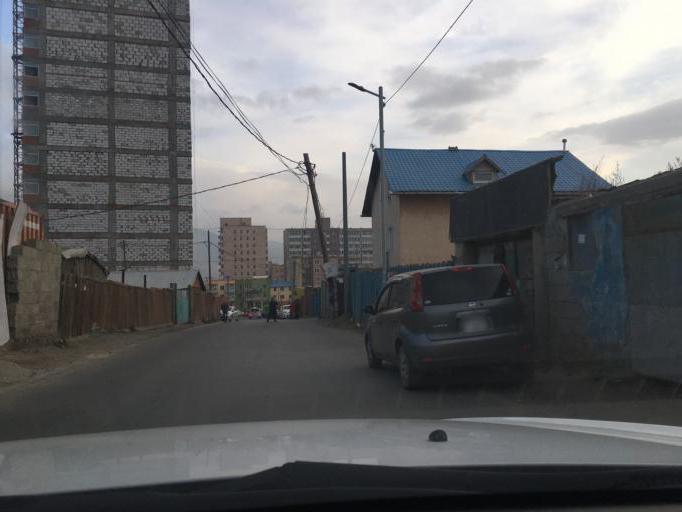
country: MN
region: Ulaanbaatar
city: Ulaanbaatar
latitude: 47.9229
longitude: 106.8574
